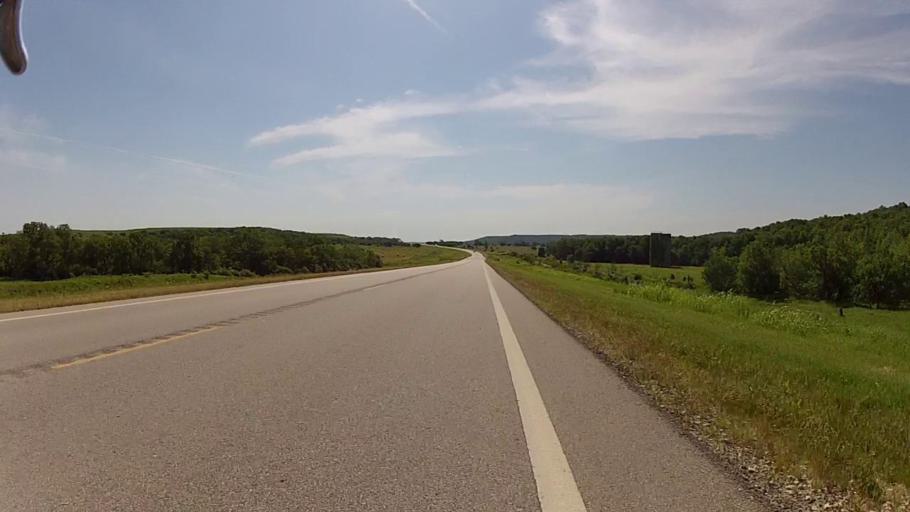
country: US
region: Kansas
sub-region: Chautauqua County
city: Sedan
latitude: 37.1091
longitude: -96.5892
